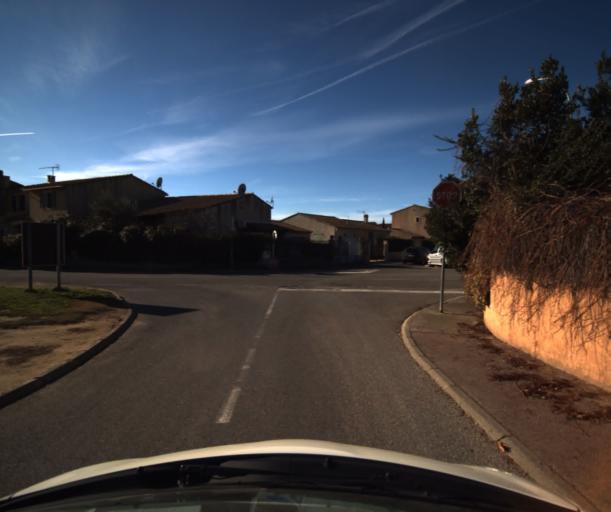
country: FR
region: Provence-Alpes-Cote d'Azur
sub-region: Departement du Vaucluse
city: Pertuis
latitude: 43.6961
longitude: 5.4865
